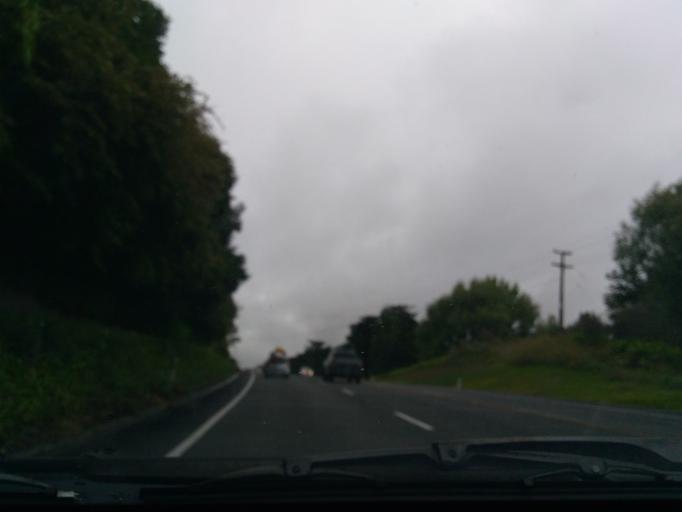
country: NZ
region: Auckland
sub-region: Auckland
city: Wellsford
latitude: -36.1498
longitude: 174.4390
